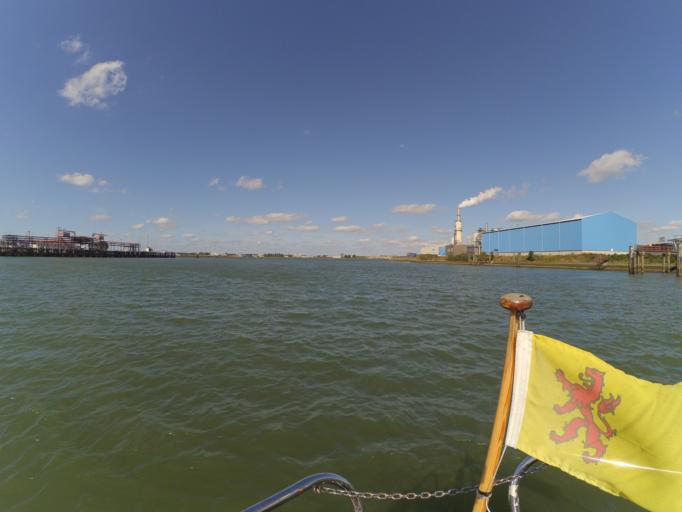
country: NL
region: South Holland
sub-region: Gemeente Vlaardingen
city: Vlaardingen
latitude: 51.8851
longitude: 4.3260
